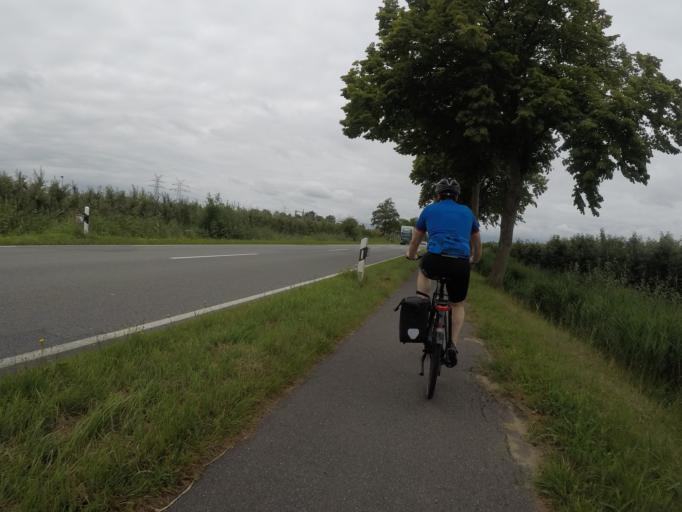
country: DE
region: Lower Saxony
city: Mittelnkirchen
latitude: 53.5394
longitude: 9.6379
